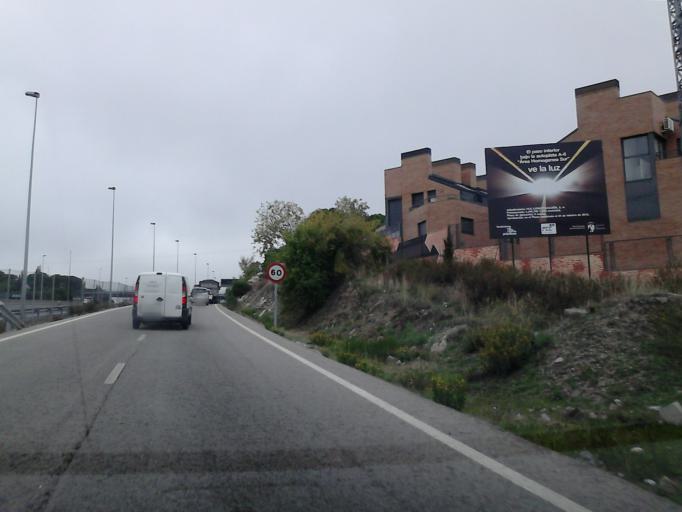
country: ES
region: Madrid
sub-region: Provincia de Madrid
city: Torrelodones
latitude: 40.5717
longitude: -3.9228
